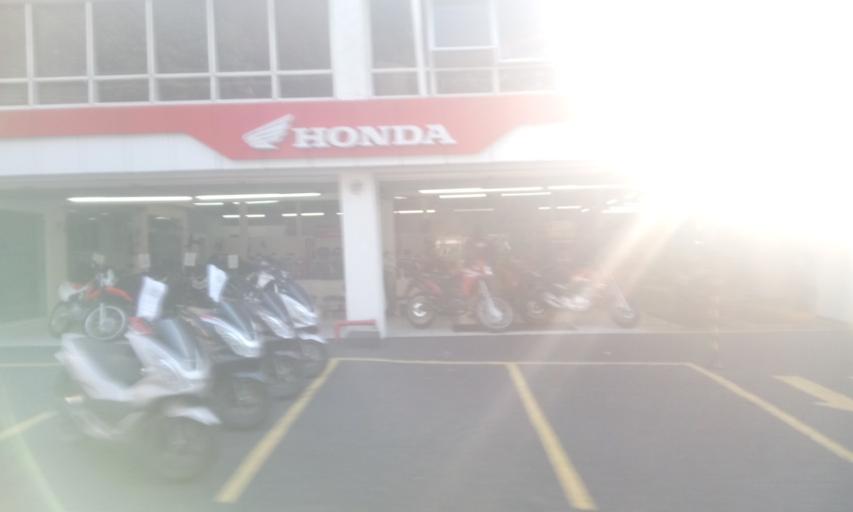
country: BR
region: Sao Paulo
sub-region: Sao Paulo
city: Sao Paulo
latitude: -23.5967
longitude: -46.6100
